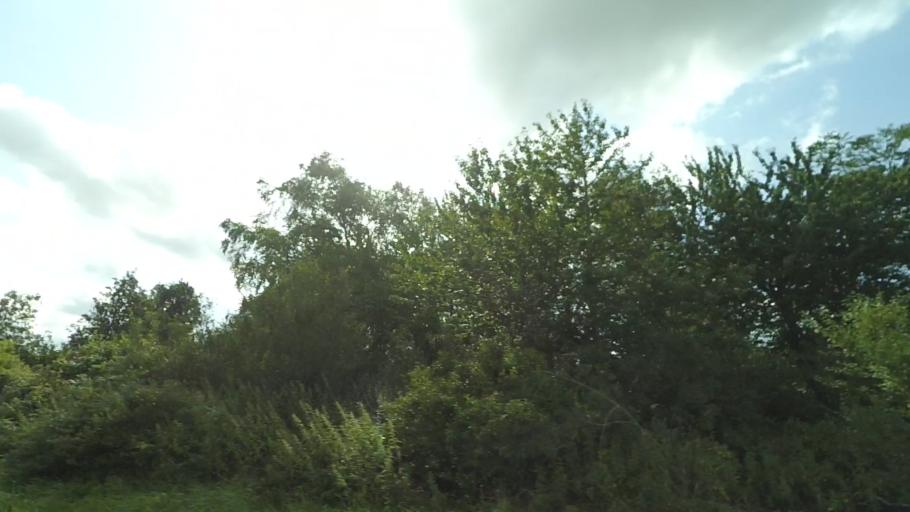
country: DK
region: Central Jutland
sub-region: Norddjurs Kommune
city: Auning
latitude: 56.4855
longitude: 10.4388
